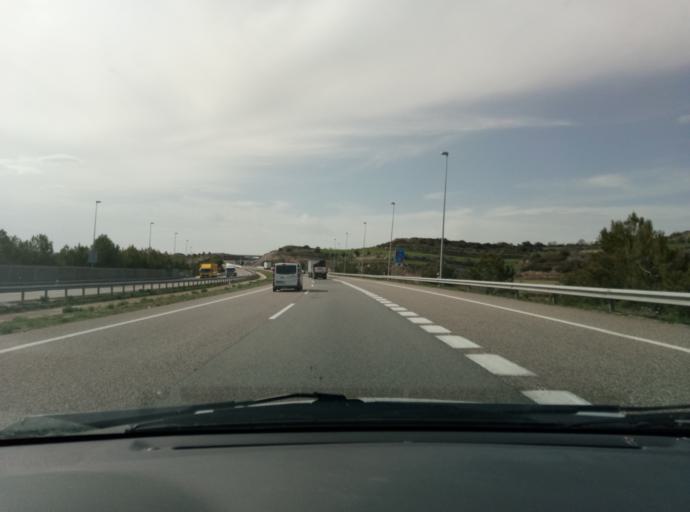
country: ES
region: Catalonia
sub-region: Provincia de Lleida
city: Cervera
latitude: 41.6650
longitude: 1.3023
